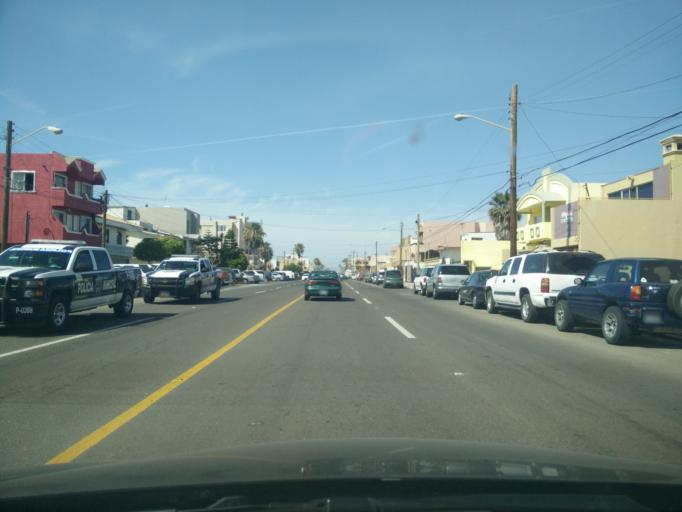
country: US
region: California
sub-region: San Diego County
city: Imperial Beach
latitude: 32.5251
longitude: -117.1231
